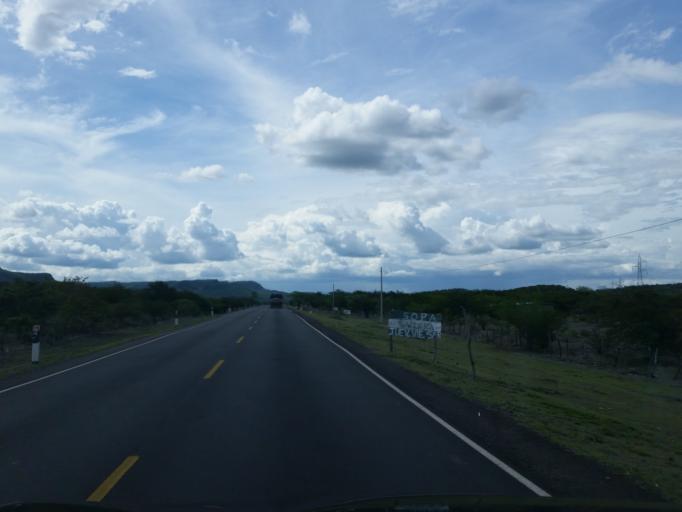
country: NI
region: Matagalpa
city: Ciudad Dario
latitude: 12.6509
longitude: -86.0735
